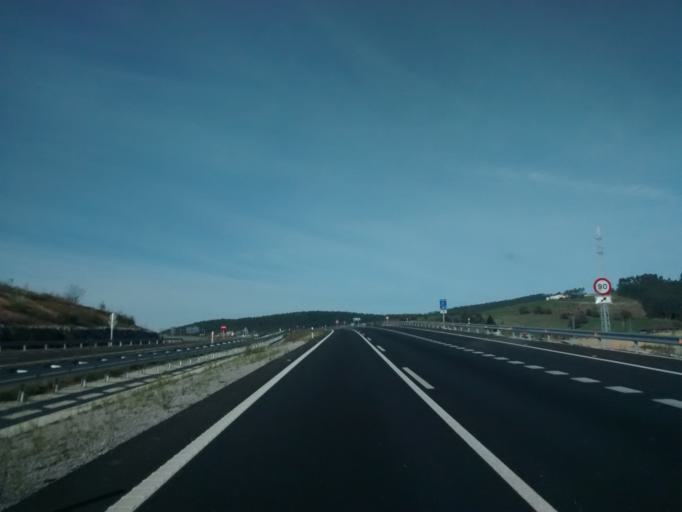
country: ES
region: Cantabria
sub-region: Provincia de Cantabria
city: Puente Viesgo
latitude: 43.3418
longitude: -3.9911
